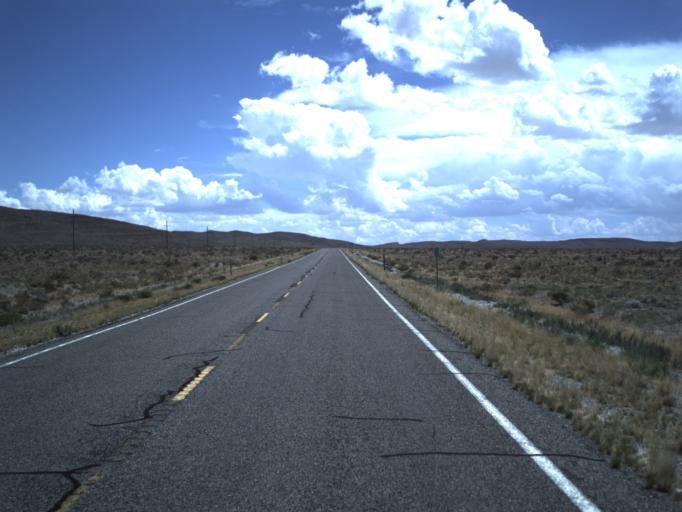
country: US
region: Utah
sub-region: Beaver County
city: Milford
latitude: 39.0312
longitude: -113.3831
